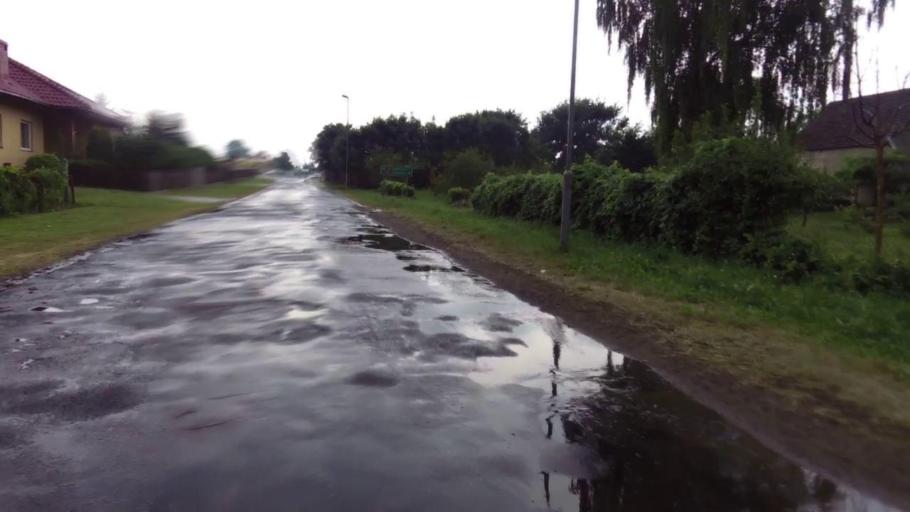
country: PL
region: West Pomeranian Voivodeship
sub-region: Powiat choszczenski
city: Recz
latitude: 53.2758
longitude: 15.4625
